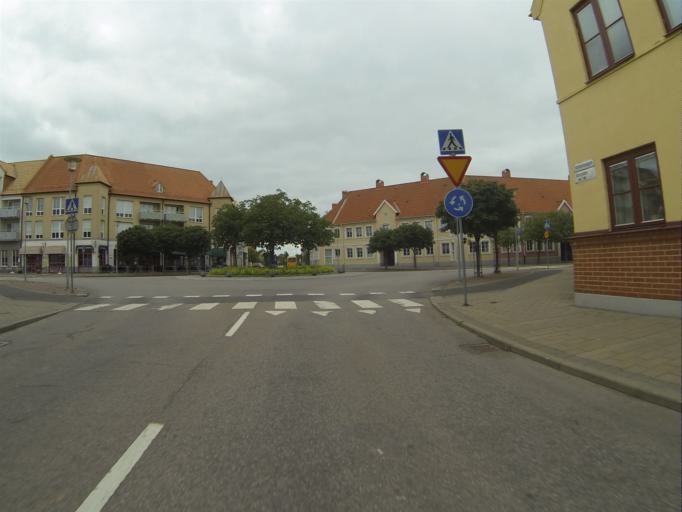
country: SE
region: Skane
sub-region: Staffanstorps Kommun
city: Staffanstorp
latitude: 55.6433
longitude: 13.2106
